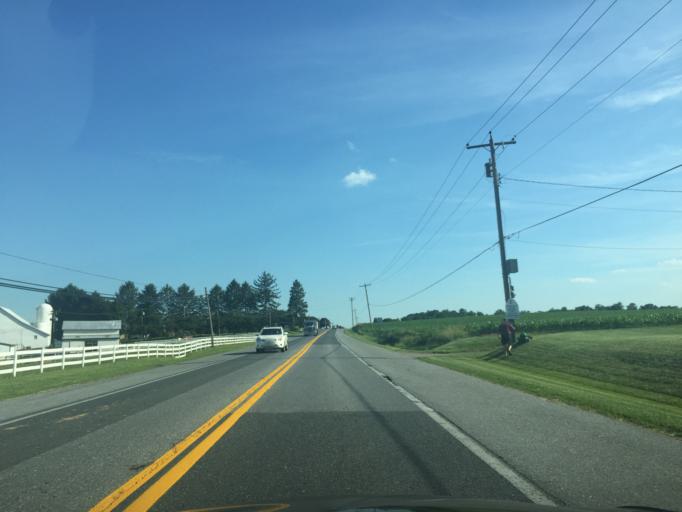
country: US
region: Maryland
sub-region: Harford County
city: Jarrettsville
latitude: 39.6211
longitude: -76.4763
